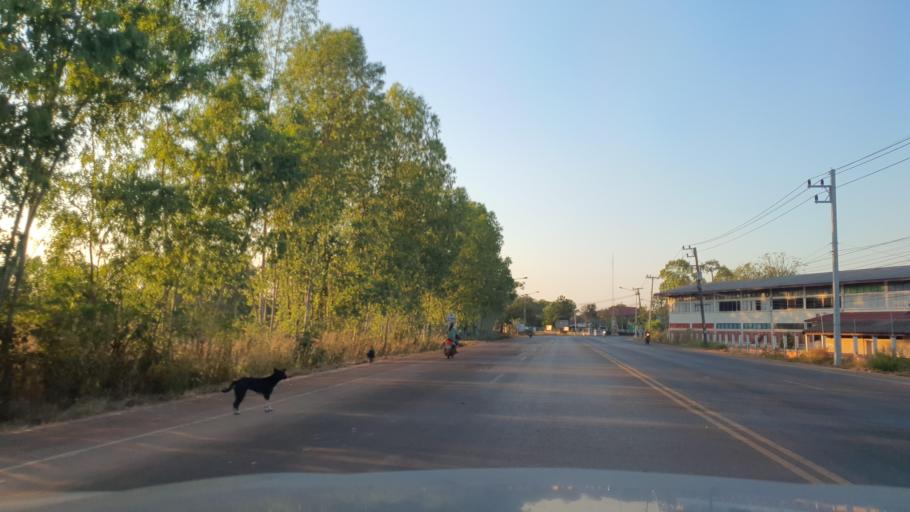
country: TH
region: Nakhon Phanom
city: Si Songkhram
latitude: 17.7646
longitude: 104.2796
